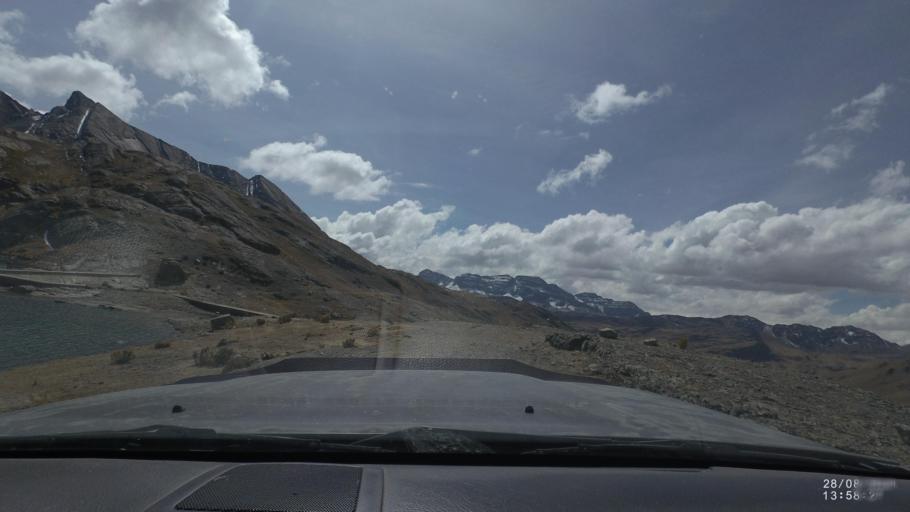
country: BO
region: Cochabamba
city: Sipe Sipe
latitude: -17.2756
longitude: -66.3878
